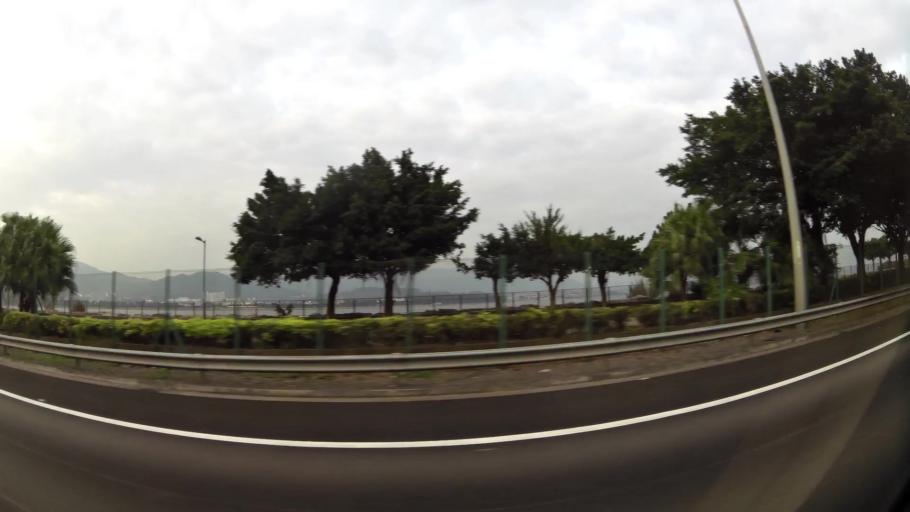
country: HK
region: Tai Po
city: Tai Po
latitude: 22.4397
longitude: 114.1863
